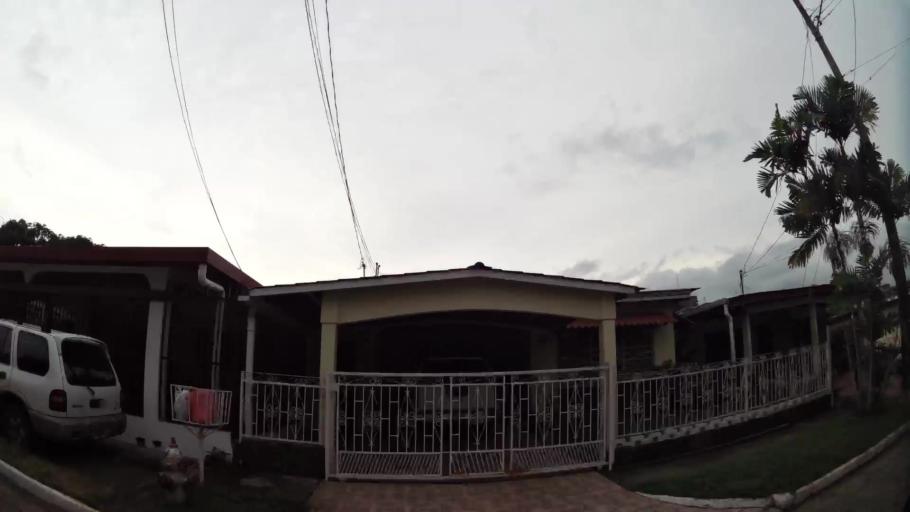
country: PA
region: Panama
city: Panama
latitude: 9.0177
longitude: -79.5273
